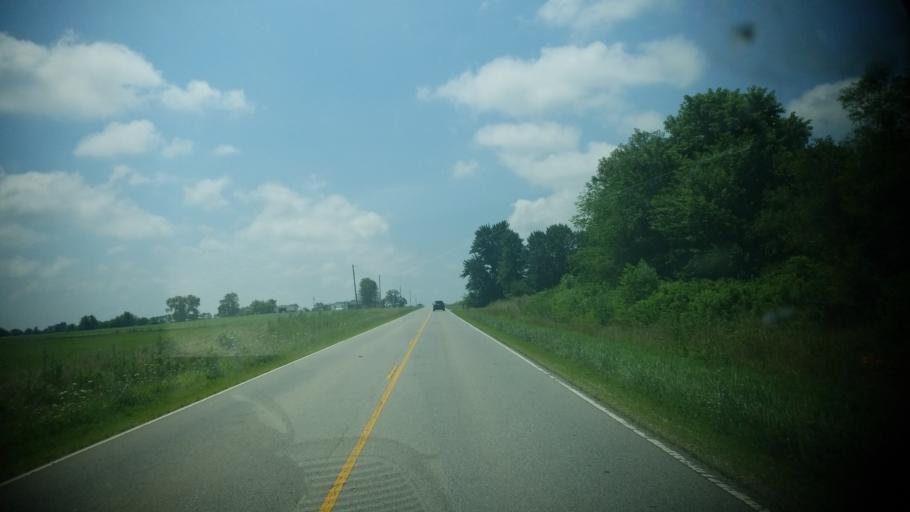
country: US
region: Illinois
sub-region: Wayne County
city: Fairfield
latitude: 38.5058
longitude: -88.3485
